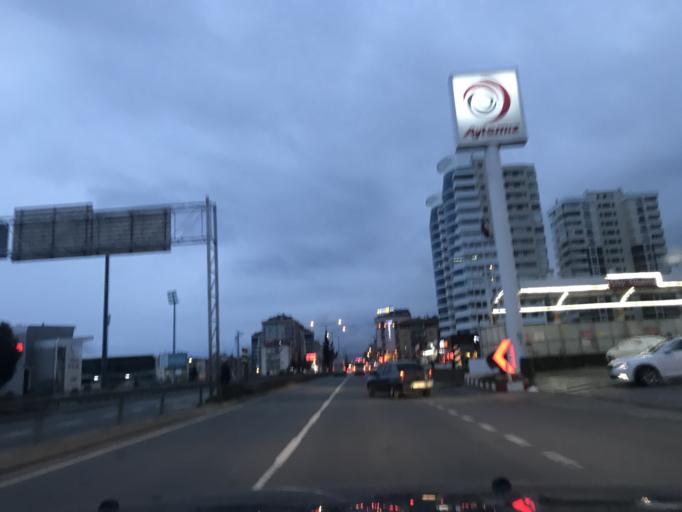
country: TR
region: Trabzon
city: Akcaabat
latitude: 41.0157
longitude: 39.5947
